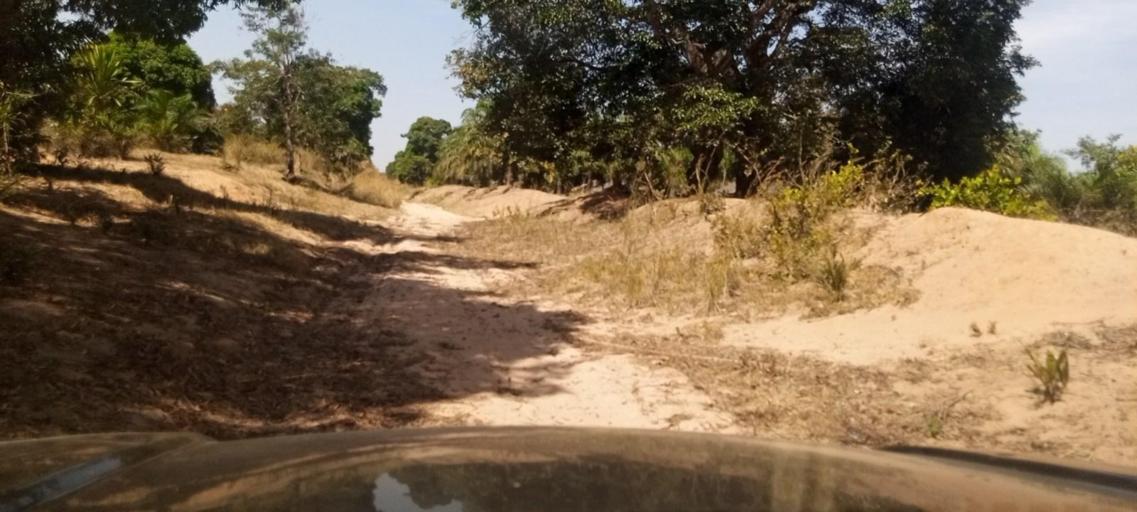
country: CD
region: Kasai-Oriental
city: Kabinda
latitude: -5.8041
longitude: 25.0182
